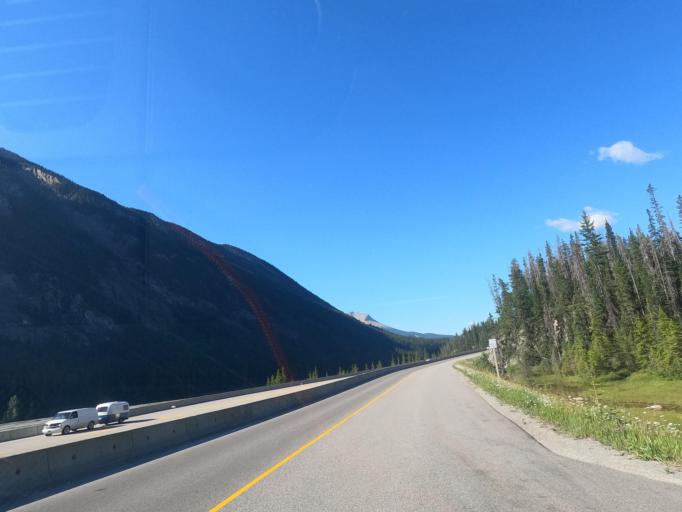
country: CA
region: Alberta
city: Lake Louise
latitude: 51.3852
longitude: -116.5036
